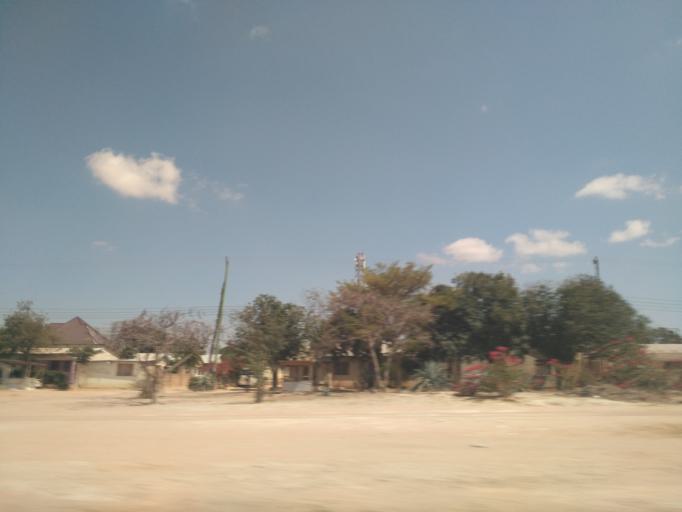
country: TZ
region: Dodoma
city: Dodoma
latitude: -6.1506
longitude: 35.7281
